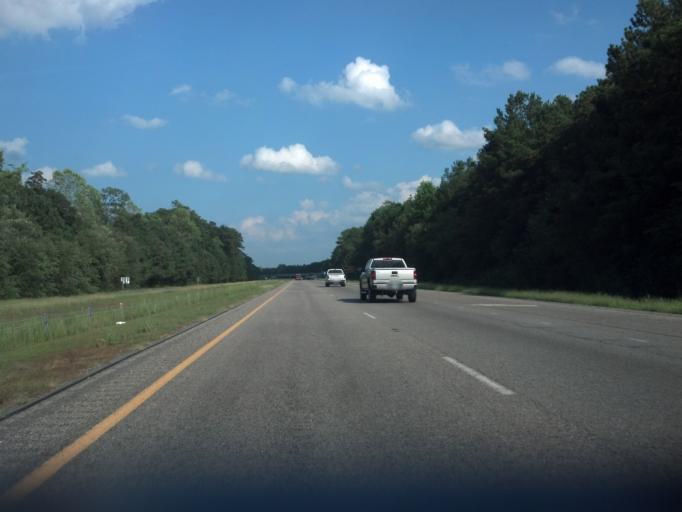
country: US
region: North Carolina
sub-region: Edgecombe County
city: Tarboro
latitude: 35.8846
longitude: -77.5798
